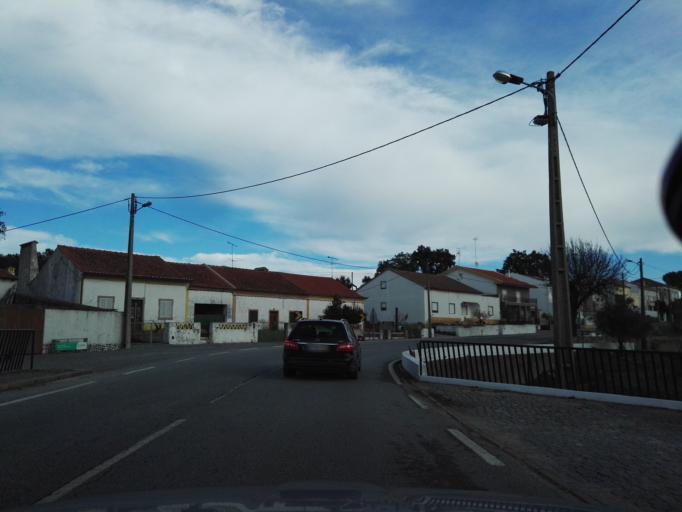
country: PT
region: Portalegre
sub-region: Nisa
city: Nisa
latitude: 39.4869
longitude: -7.7233
